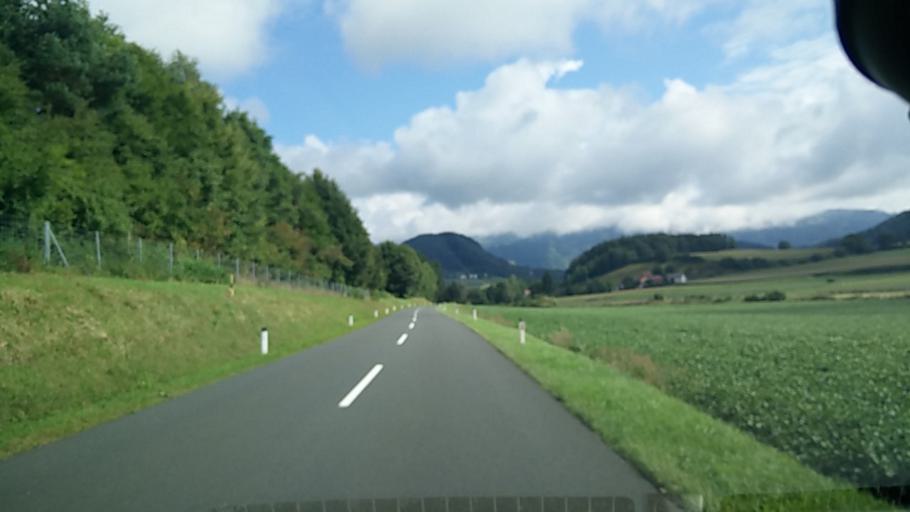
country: AT
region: Carinthia
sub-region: Politischer Bezirk Volkermarkt
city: Voelkermarkt
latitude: 46.6626
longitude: 14.5735
